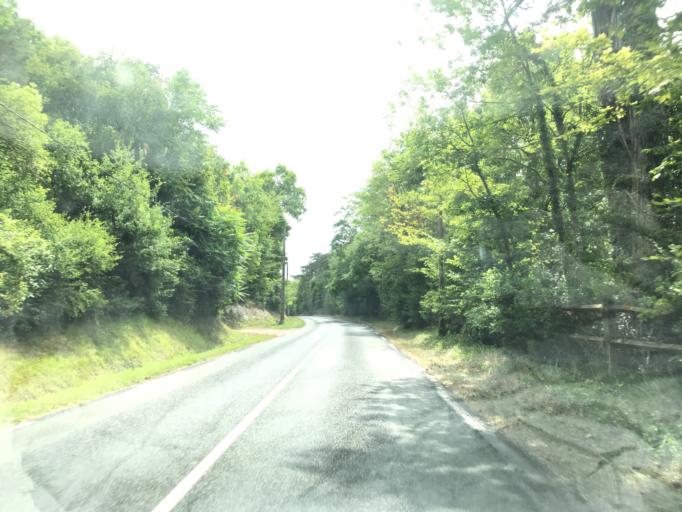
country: FR
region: Haute-Normandie
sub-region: Departement de l'Eure
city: Houlbec-Cocherel
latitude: 49.0632
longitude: 1.3239
